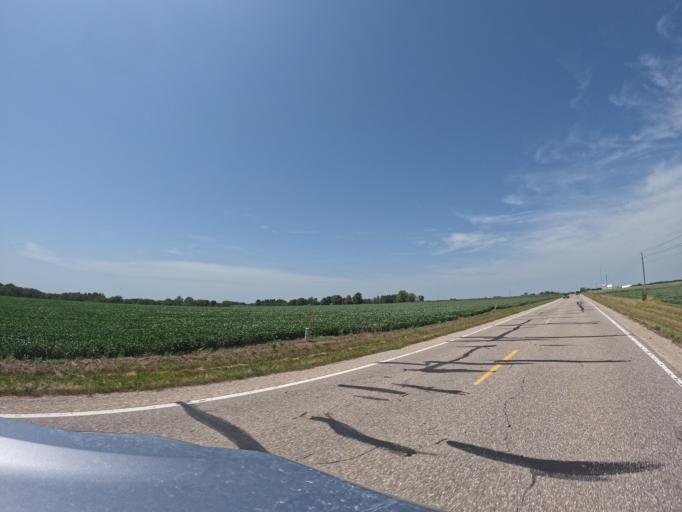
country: US
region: Iowa
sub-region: Henry County
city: Mount Pleasant
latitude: 40.9935
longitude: -91.6122
